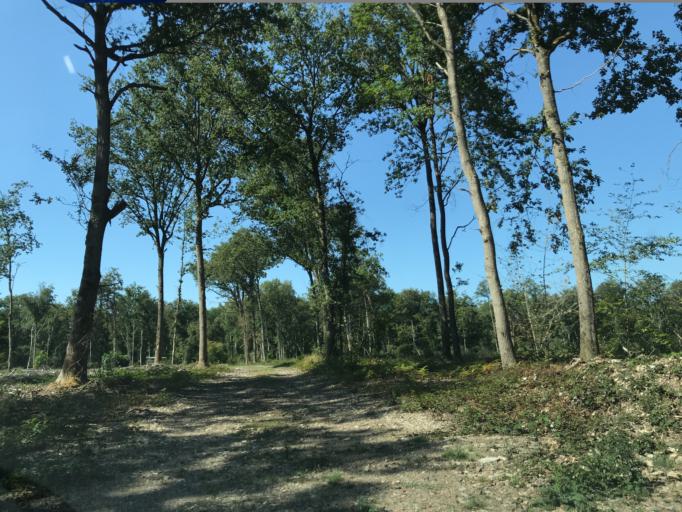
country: FR
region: Haute-Normandie
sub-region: Departement de l'Eure
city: Heudreville-sur-Eure
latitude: 49.1074
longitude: 1.2056
